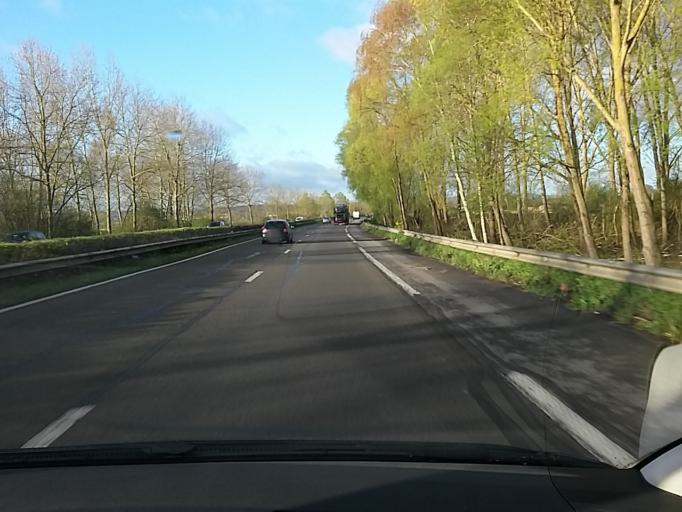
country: FR
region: Picardie
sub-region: Departement de l'Oise
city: Longueil-Sainte-Marie
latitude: 49.3426
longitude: 2.7377
